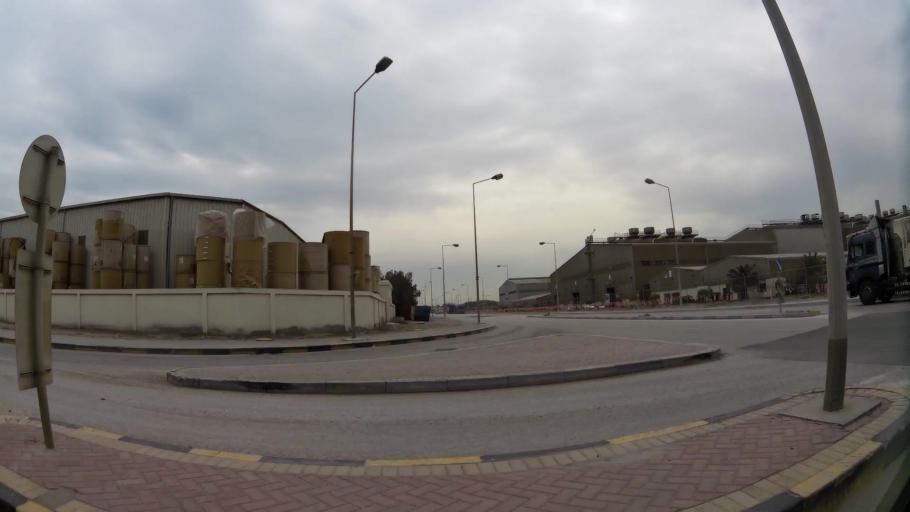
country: BH
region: Northern
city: Sitrah
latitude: 26.1832
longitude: 50.6155
